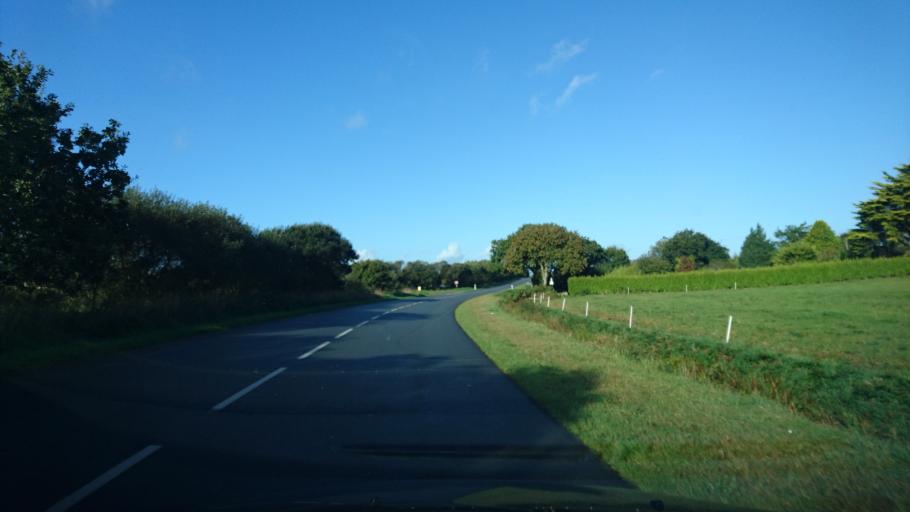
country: FR
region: Brittany
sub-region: Departement du Finistere
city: Plouarzel
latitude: 48.4383
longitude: -4.7304
